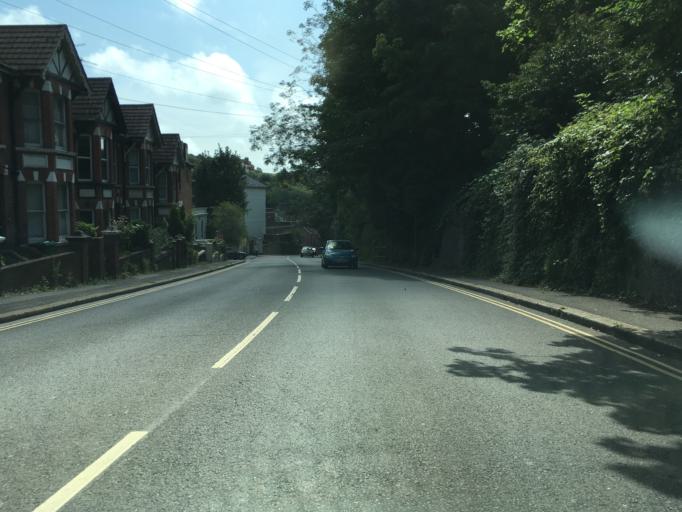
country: GB
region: England
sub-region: East Sussex
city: Hastings
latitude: 50.8646
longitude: 0.5976
